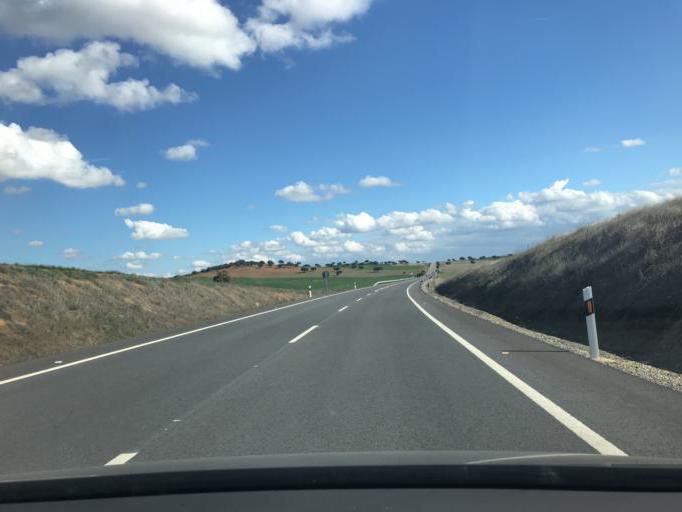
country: ES
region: Extremadura
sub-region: Provincia de Badajoz
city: Granja de Torrehermosa
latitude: 38.2971
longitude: -5.5524
